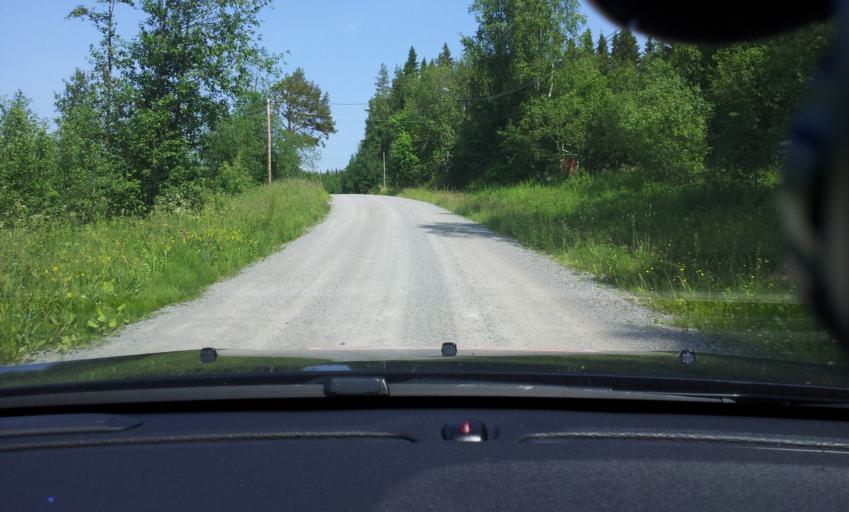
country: SE
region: Jaemtland
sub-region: Bergs Kommun
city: Hoverberg
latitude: 62.7840
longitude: 14.4525
